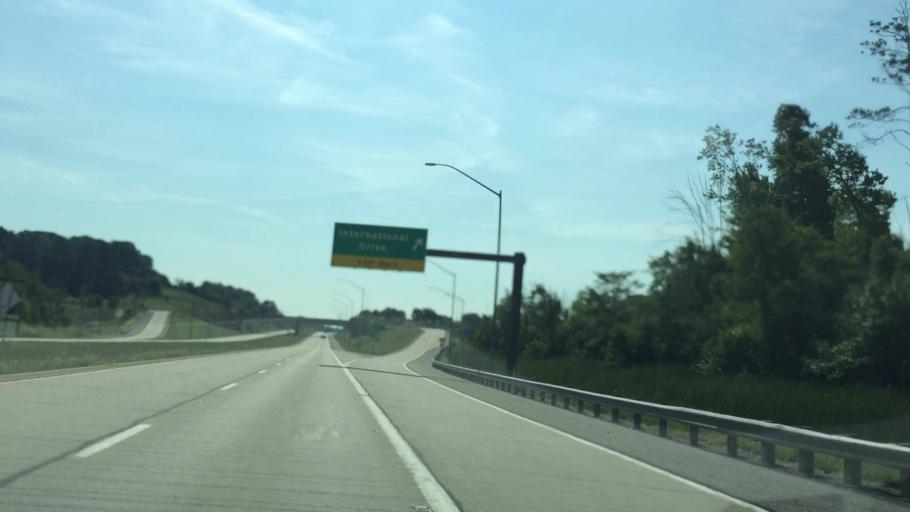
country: US
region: Pennsylvania
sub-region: Allegheny County
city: Carnot-Moon
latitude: 40.5102
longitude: -80.2572
